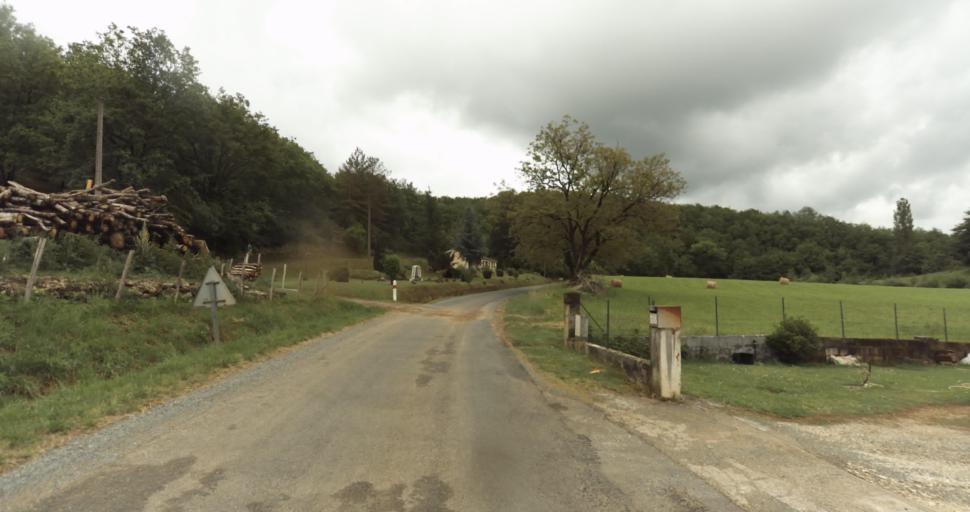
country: FR
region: Aquitaine
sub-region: Departement de la Dordogne
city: Belves
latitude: 44.7608
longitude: 0.9065
